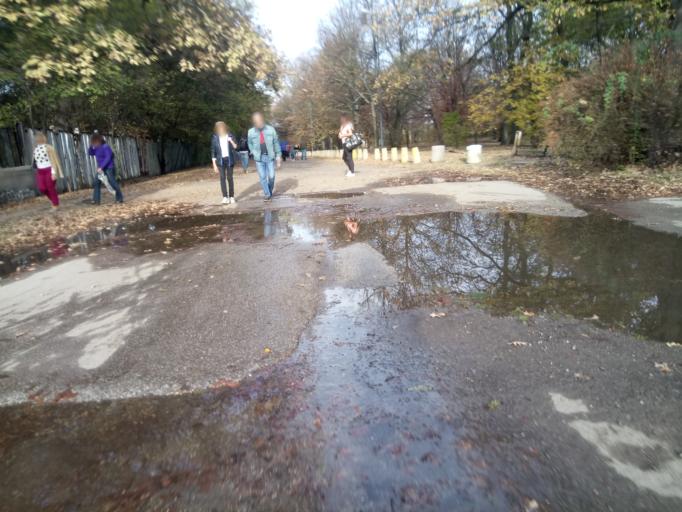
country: BG
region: Sofia-Capital
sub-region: Stolichna Obshtina
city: Sofia
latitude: 42.6807
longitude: 23.3443
